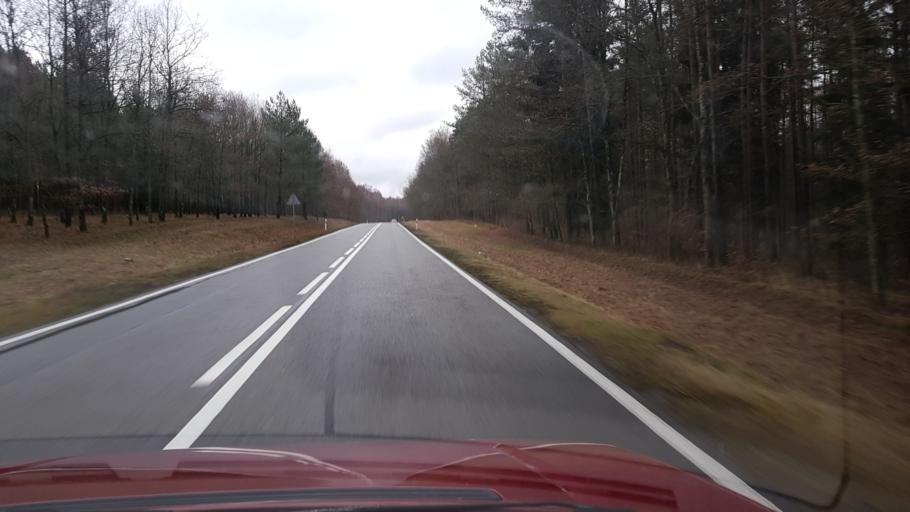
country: PL
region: West Pomeranian Voivodeship
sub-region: Powiat drawski
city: Drawsko Pomorskie
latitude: 53.4953
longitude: 15.6979
